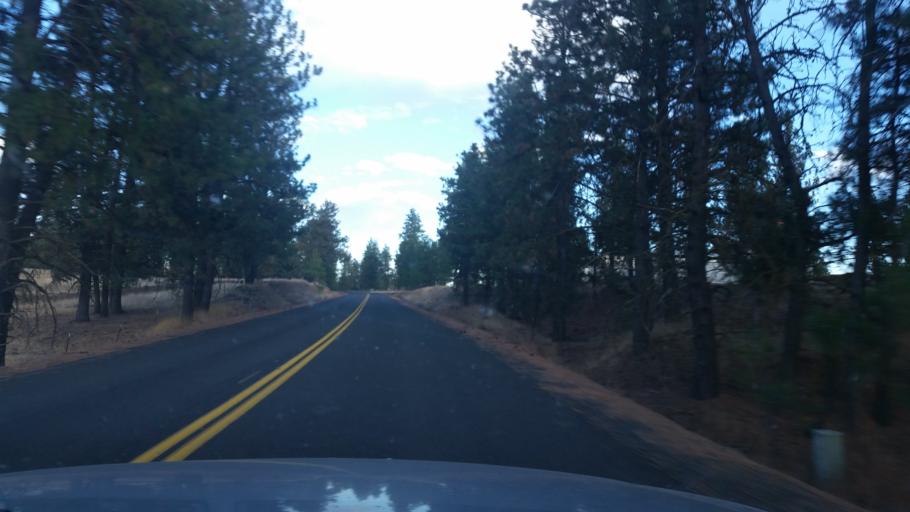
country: US
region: Washington
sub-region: Spokane County
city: Medical Lake
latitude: 47.4499
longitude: -117.7949
